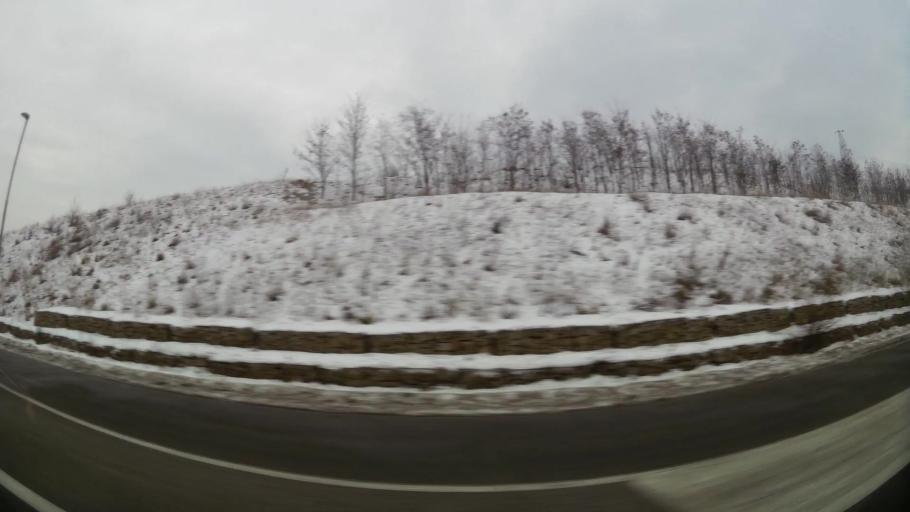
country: MK
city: Kondovo
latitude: 42.0363
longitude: 21.3347
